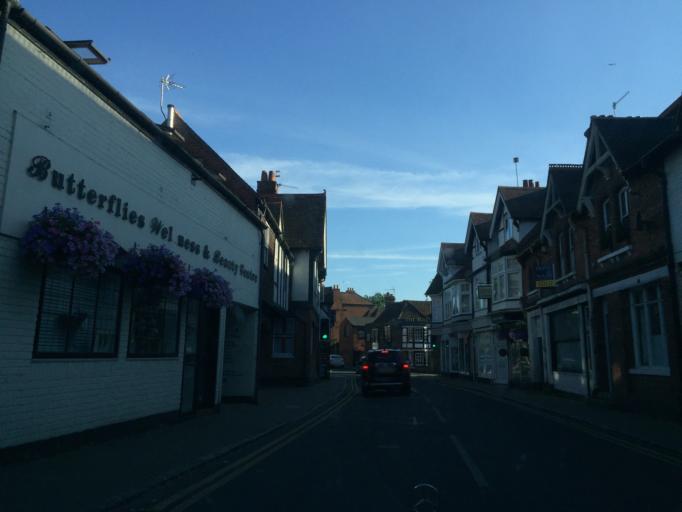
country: GB
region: England
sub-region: Wokingham
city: Wargrave
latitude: 51.5011
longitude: -0.8698
